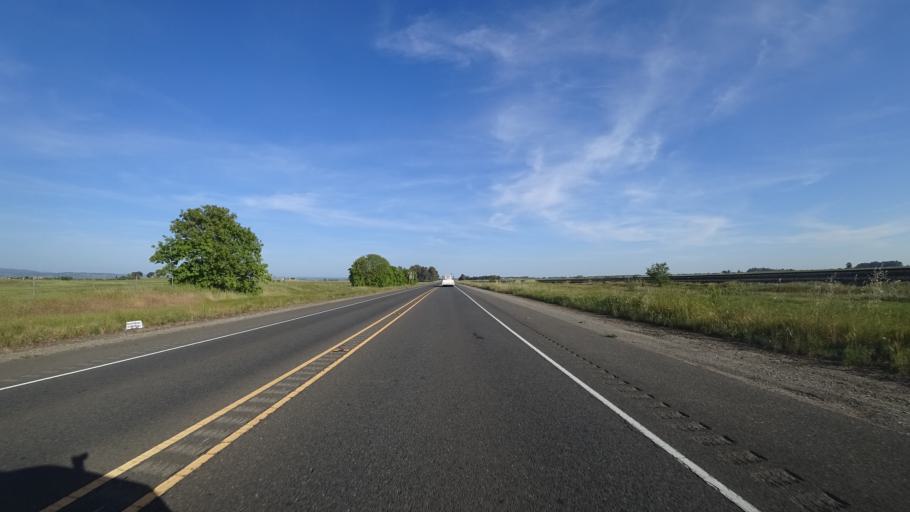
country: US
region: California
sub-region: Placer County
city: Sheridan
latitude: 38.9764
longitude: -121.3728
